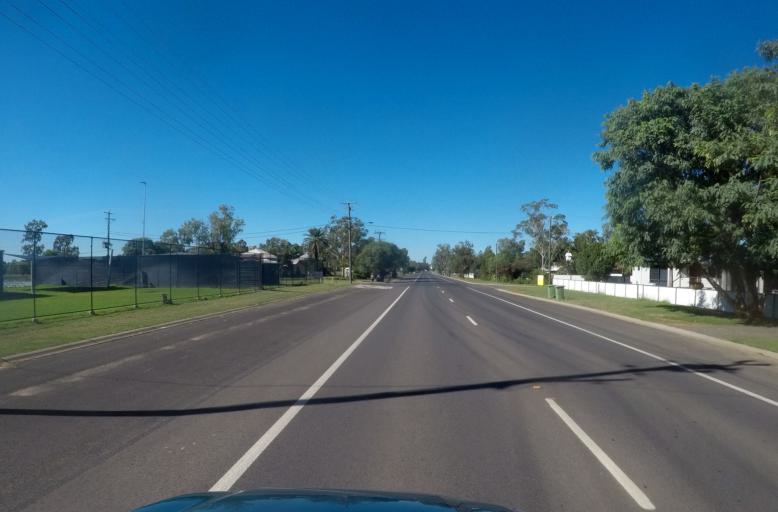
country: AU
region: Queensland
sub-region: Maranoa
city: Roma
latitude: -26.5573
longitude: 148.7858
